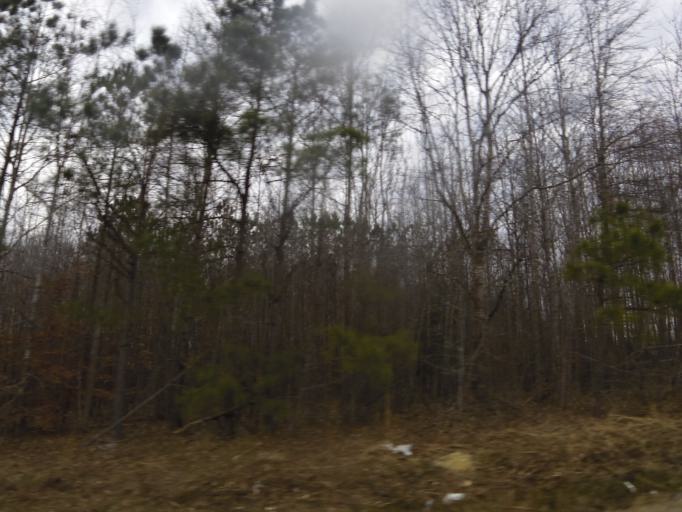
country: US
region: North Carolina
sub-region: Hertford County
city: Murfreesboro
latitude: 36.3602
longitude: -77.1744
